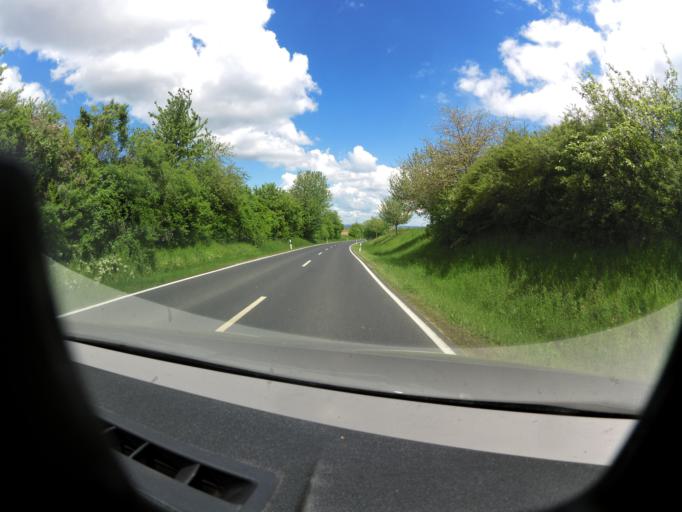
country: DE
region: Bavaria
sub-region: Regierungsbezirk Unterfranken
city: Waigolshausen
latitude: 49.9540
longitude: 10.1455
